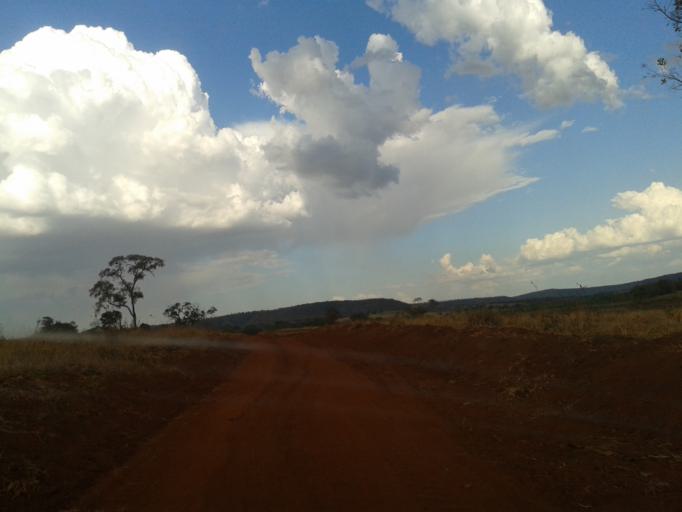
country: BR
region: Minas Gerais
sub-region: Santa Vitoria
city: Santa Vitoria
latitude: -19.1709
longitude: -49.9443
